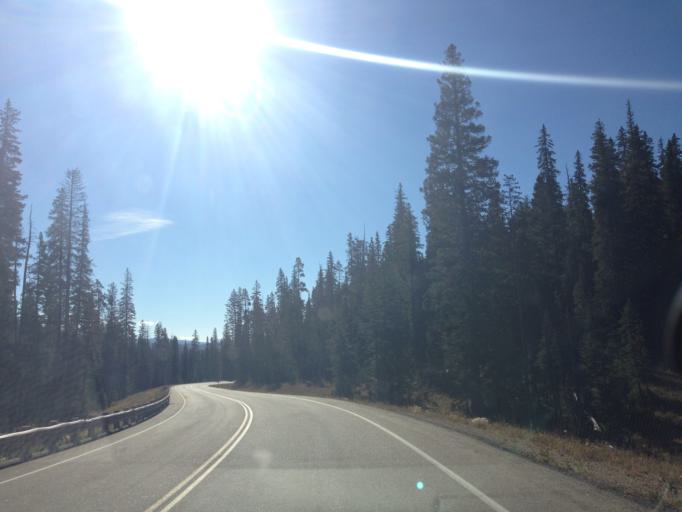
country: US
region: Montana
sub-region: Carbon County
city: Red Lodge
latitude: 45.0082
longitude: -109.8641
